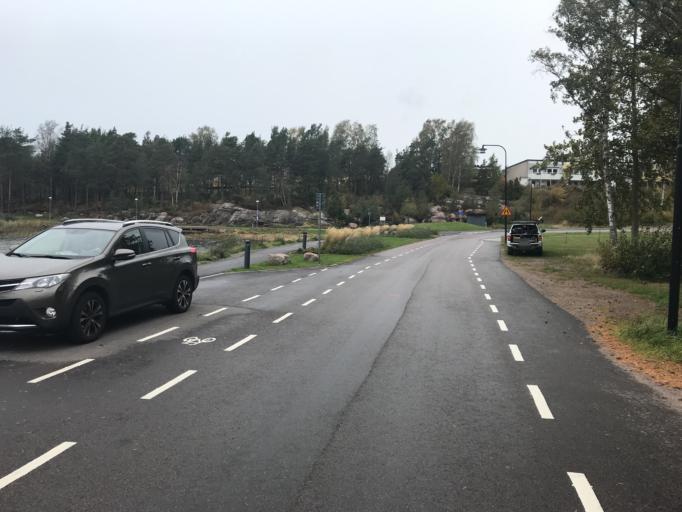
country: SE
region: Vaermland
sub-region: Hammaro Kommun
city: Skoghall
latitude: 59.3182
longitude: 13.4631
